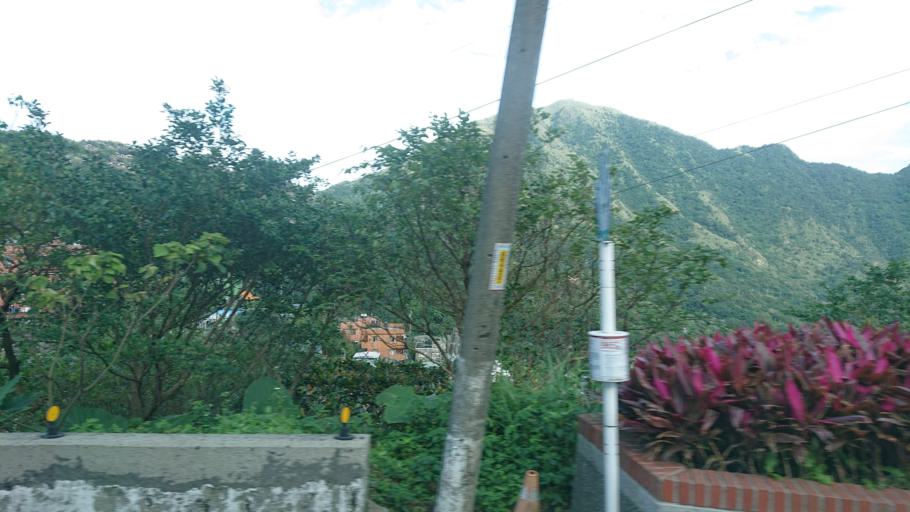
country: TW
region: Taiwan
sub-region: Keelung
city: Keelung
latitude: 25.1077
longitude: 121.8527
